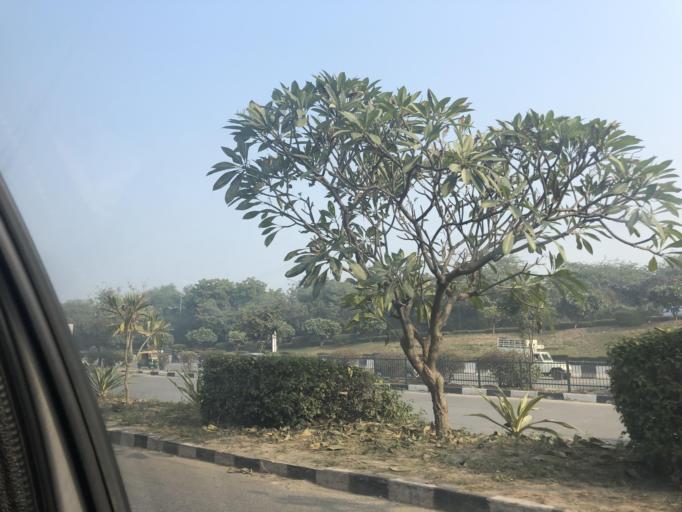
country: IN
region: NCT
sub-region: Central Delhi
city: Karol Bagh
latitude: 28.5973
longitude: 77.1642
